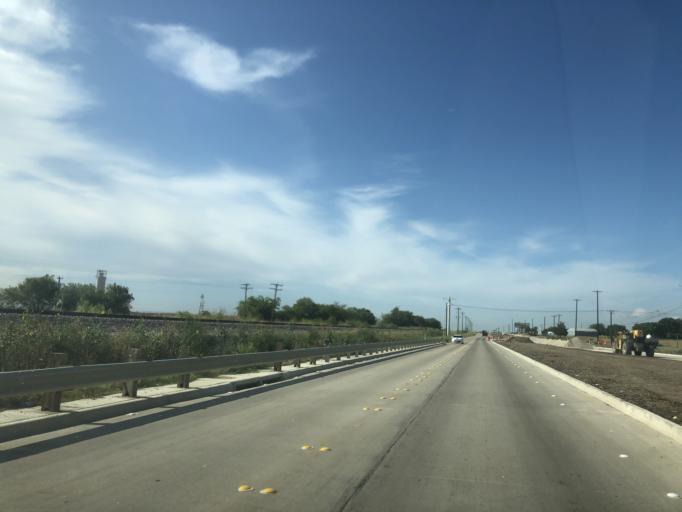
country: US
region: Texas
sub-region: Denton County
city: Justin
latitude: 33.0442
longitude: -97.3043
